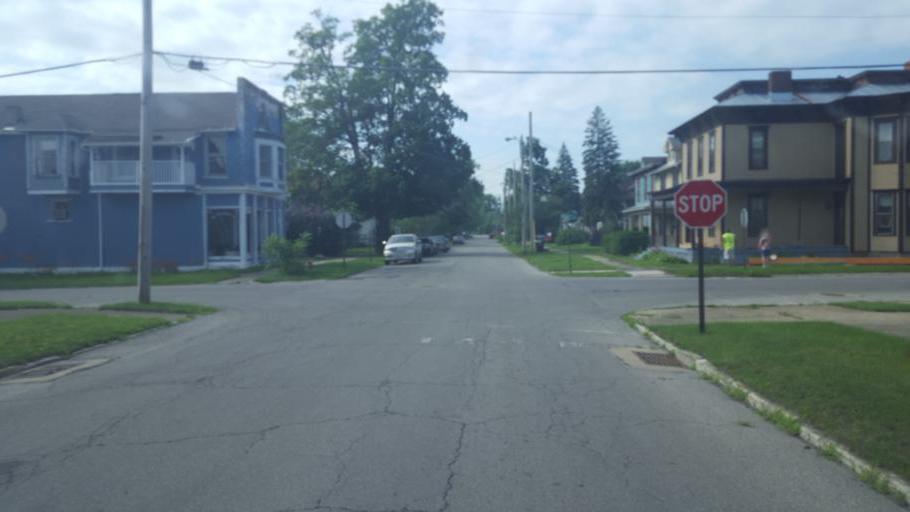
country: US
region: Ohio
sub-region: Crawford County
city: Galion
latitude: 40.7327
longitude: -82.7878
